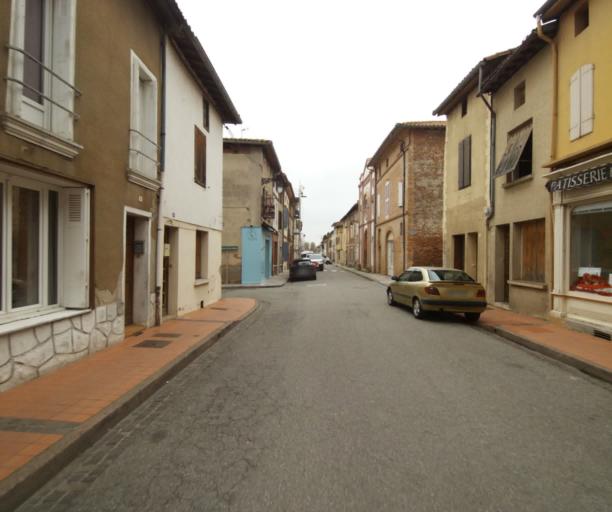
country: FR
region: Midi-Pyrenees
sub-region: Departement de l'Ariege
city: Mazeres
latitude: 43.2511
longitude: 1.6789
